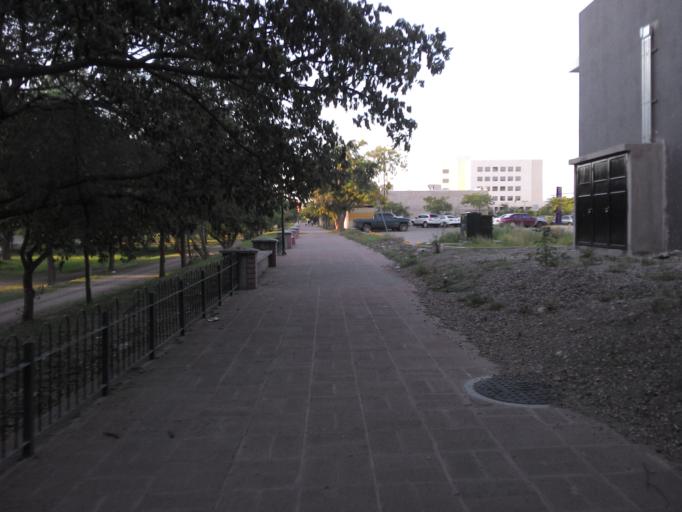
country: MX
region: Sinaloa
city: Culiacan
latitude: 24.8178
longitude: -107.4027
